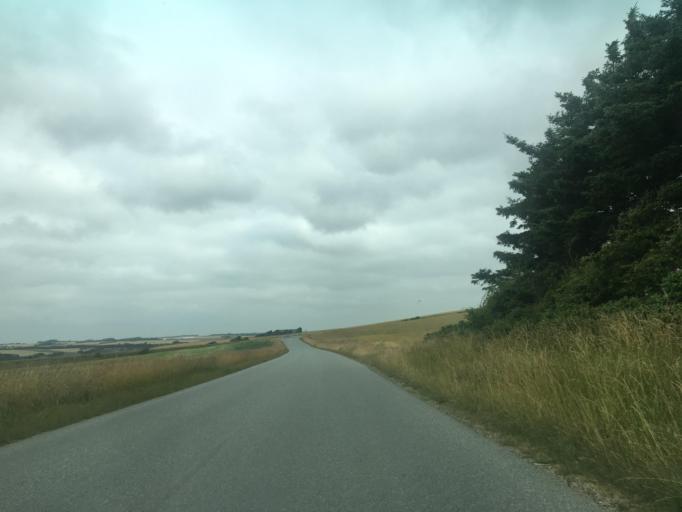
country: DK
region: North Denmark
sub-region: Thisted Kommune
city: Hurup
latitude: 56.7559
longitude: 8.4381
